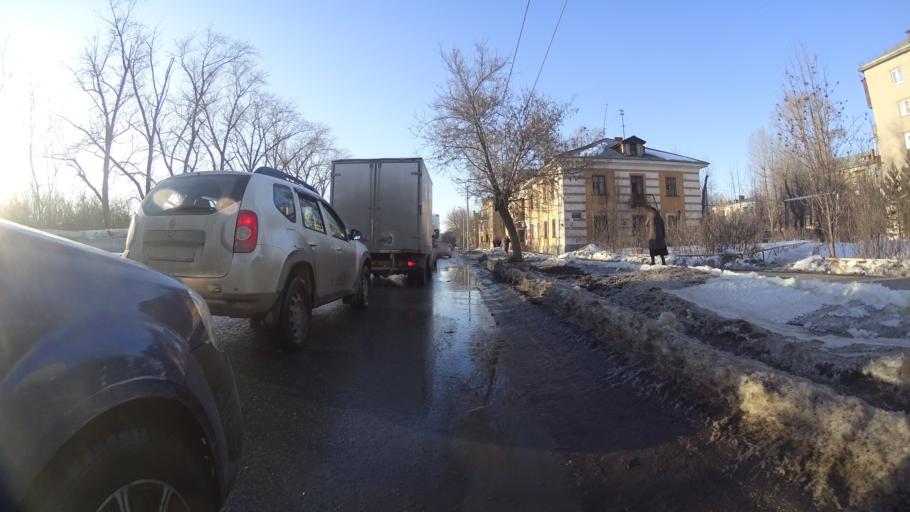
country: RU
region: Chelyabinsk
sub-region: Gorod Chelyabinsk
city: Chelyabinsk
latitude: 55.1347
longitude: 61.4582
